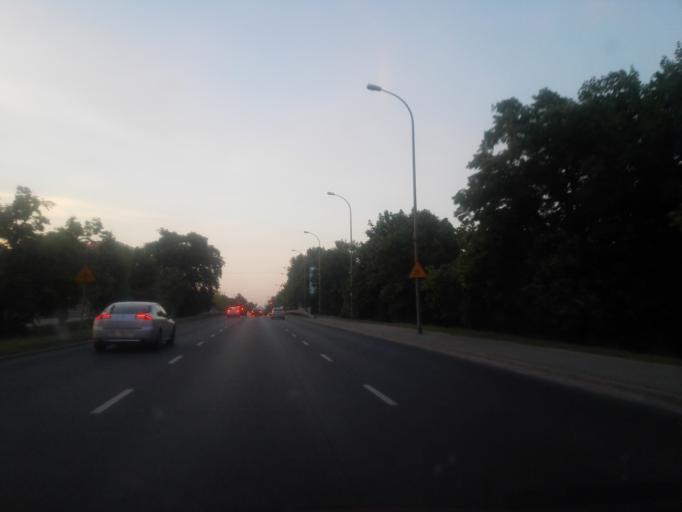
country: PL
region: Masovian Voivodeship
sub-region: Warszawa
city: Ochota
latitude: 52.1920
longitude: 20.9819
